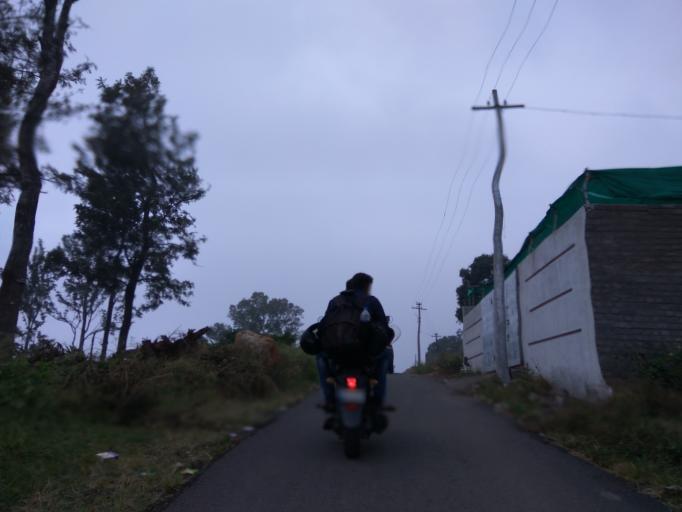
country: IN
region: Tamil Nadu
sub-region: Salem
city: Salem
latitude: 11.7676
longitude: 78.2396
